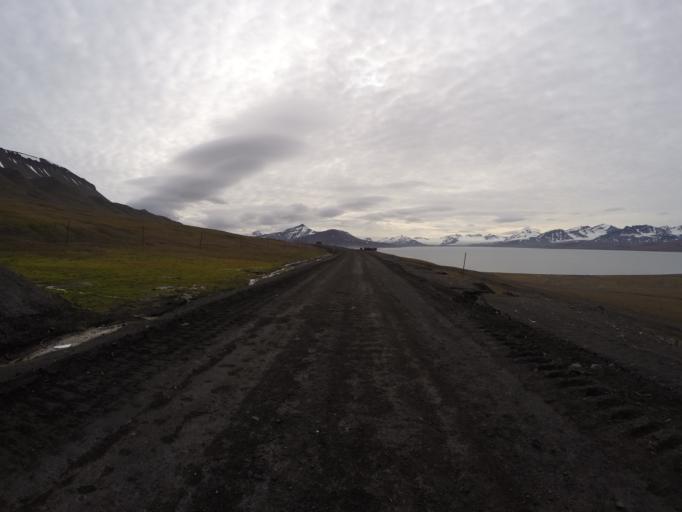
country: SJ
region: Svalbard
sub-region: Spitsbergen
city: Longyearbyen
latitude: 78.0472
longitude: 14.2281
